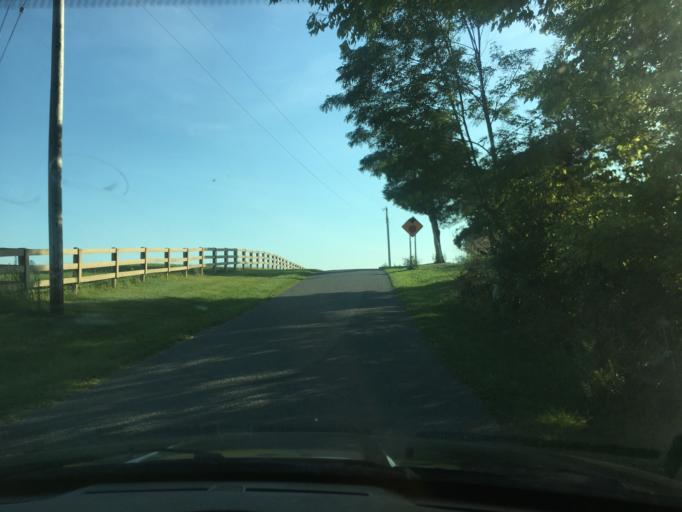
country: US
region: Ohio
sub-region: Logan County
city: West Liberty
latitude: 40.2518
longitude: -83.6626
